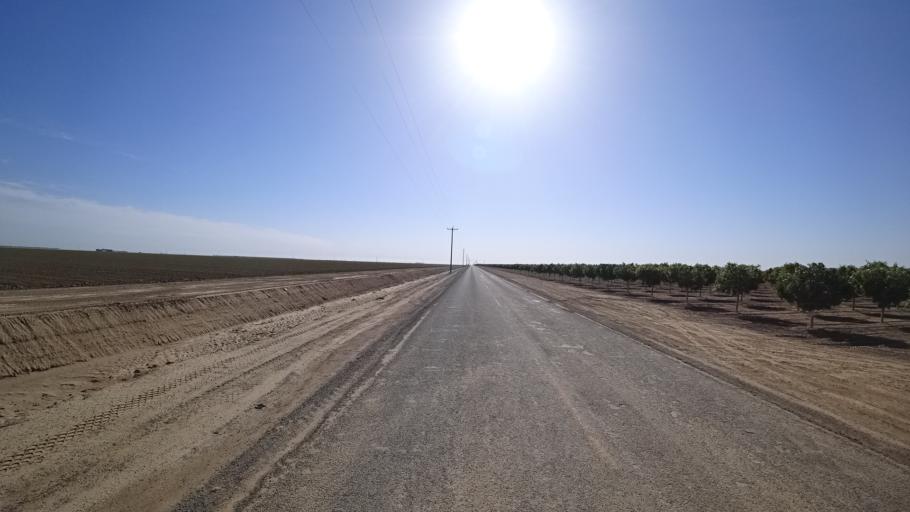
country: US
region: California
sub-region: Kings County
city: Kettleman City
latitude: 36.1088
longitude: -120.0124
